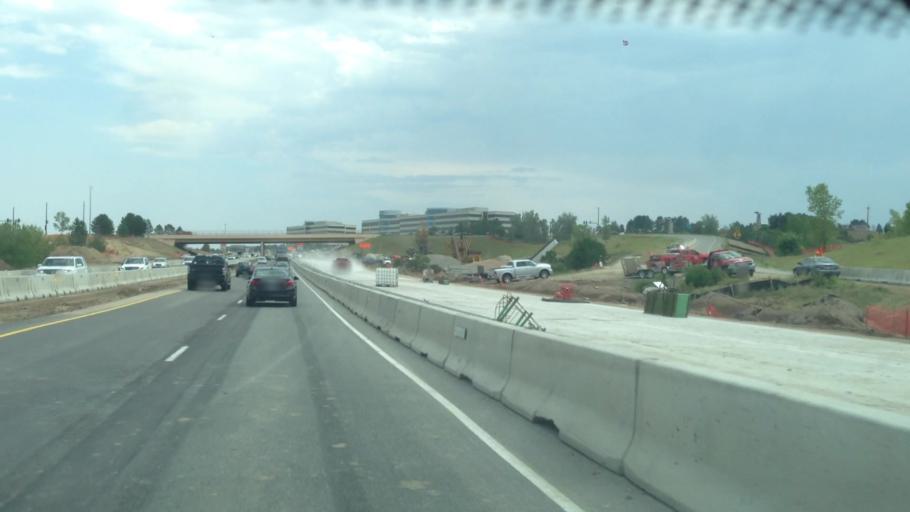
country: US
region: Colorado
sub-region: Douglas County
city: Highlands Ranch
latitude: 39.5611
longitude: -105.0122
